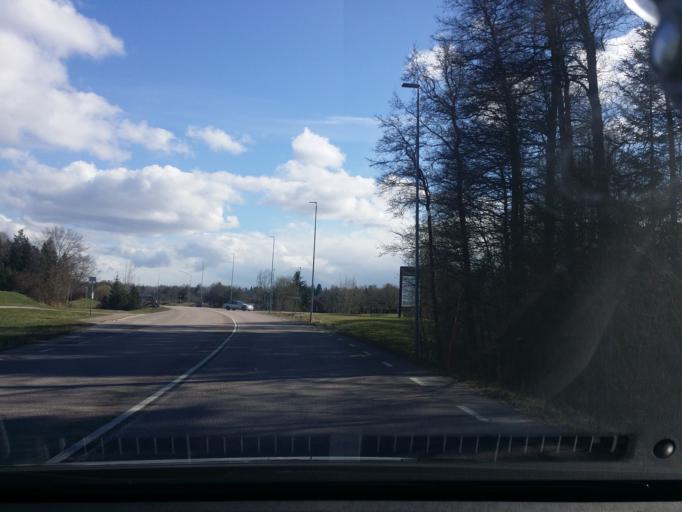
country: SE
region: Vaestmanland
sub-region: Sala Kommun
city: Sala
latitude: 59.9291
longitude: 16.5721
